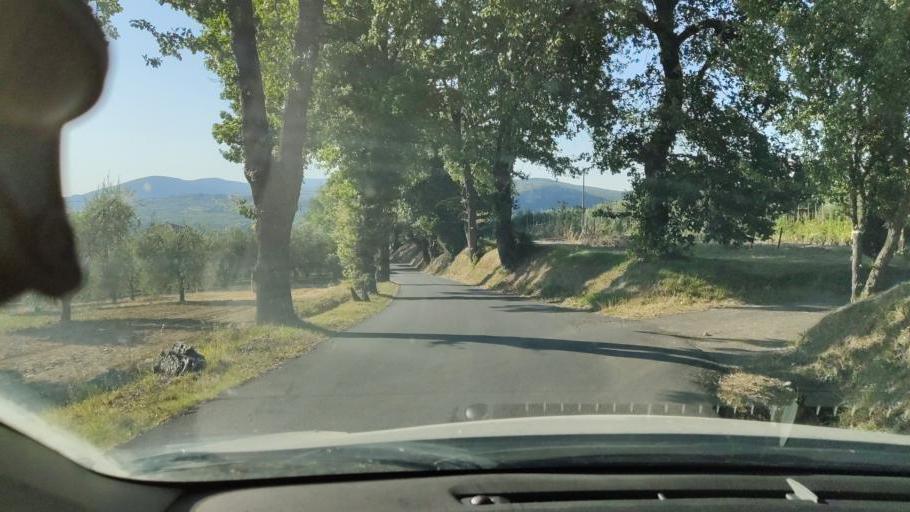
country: IT
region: Umbria
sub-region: Provincia di Terni
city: Amelia
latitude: 42.5409
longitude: 12.4017
